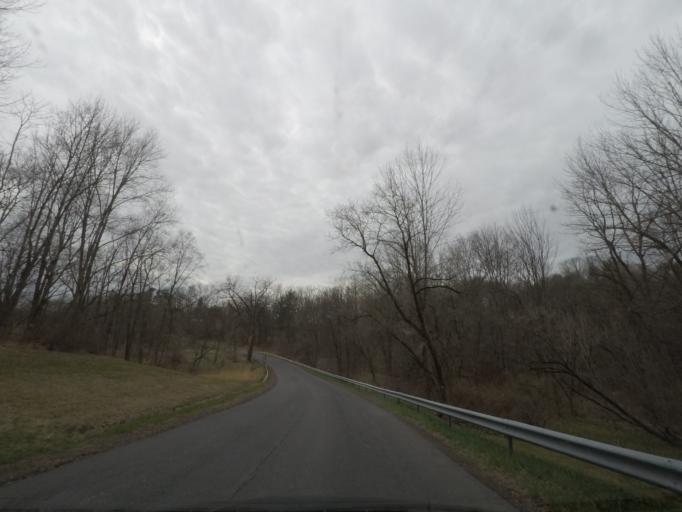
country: US
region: New York
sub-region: Rensselaer County
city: Castleton-on-Hudson
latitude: 42.5624
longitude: -73.8012
